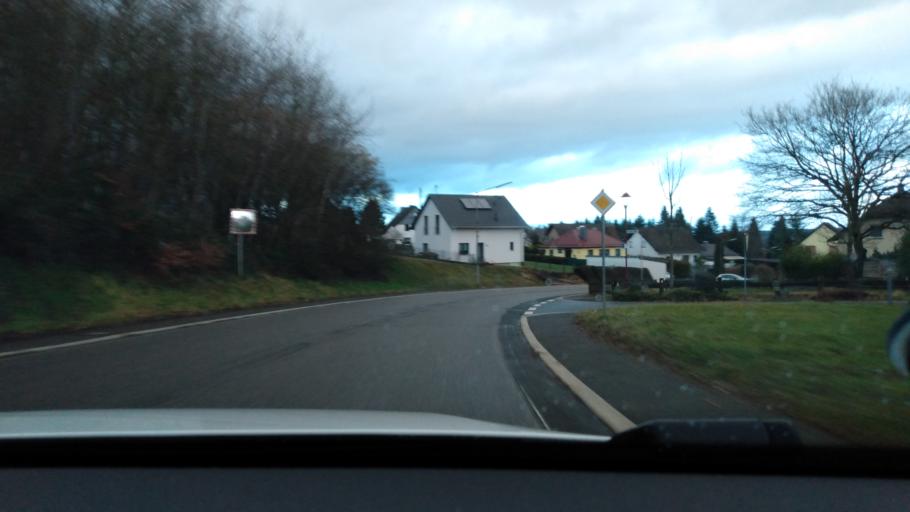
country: DE
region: Rheinland-Pfalz
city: Vettelschoss
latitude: 50.6169
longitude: 7.3155
